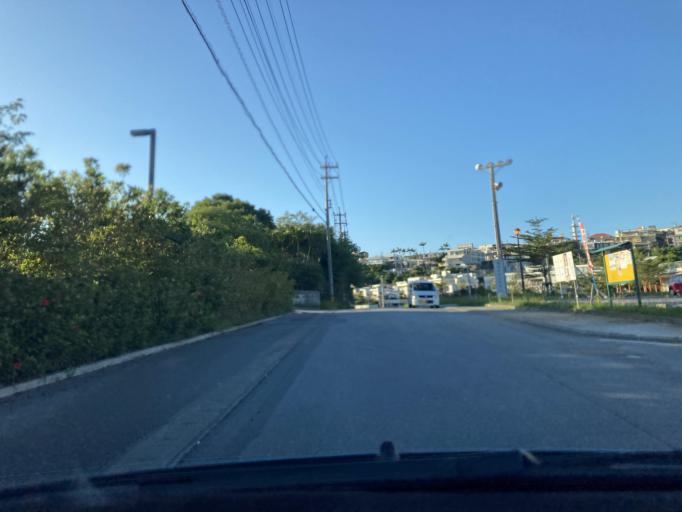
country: JP
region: Okinawa
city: Naha-shi
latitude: 26.2133
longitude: 127.7285
